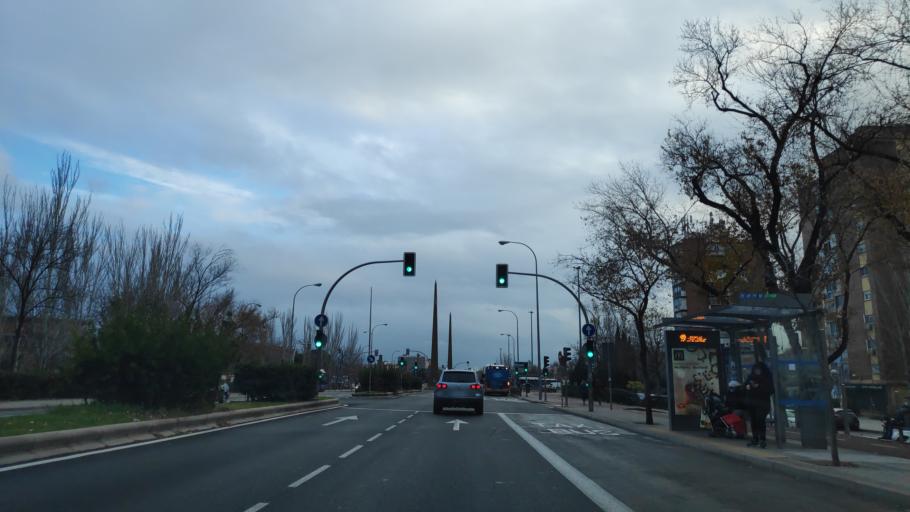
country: ES
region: Madrid
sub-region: Provincia de Madrid
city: Villaverde
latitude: 40.3528
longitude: -3.6931
